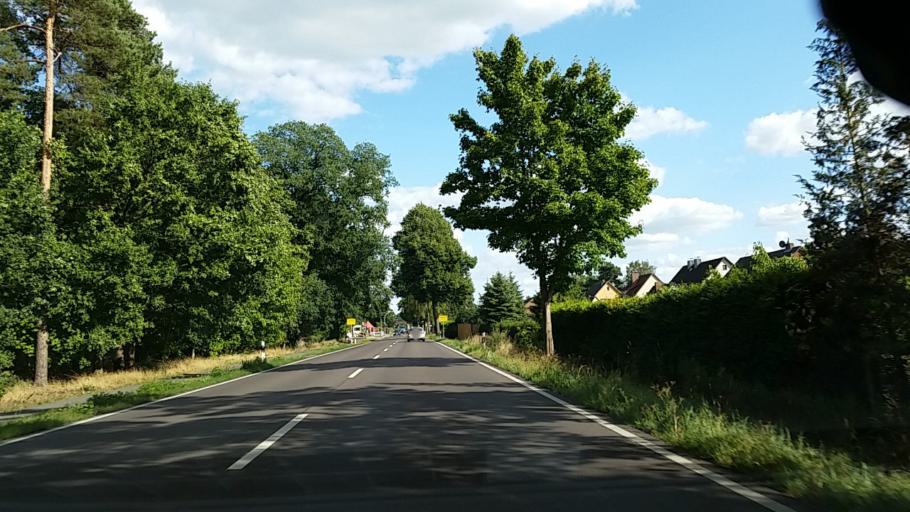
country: DE
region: Lower Saxony
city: Sassenburg
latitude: 52.4960
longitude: 10.6179
